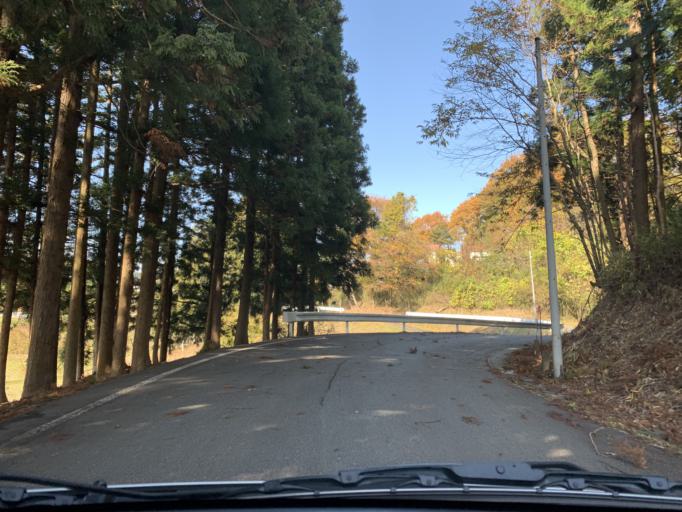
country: JP
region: Iwate
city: Ichinoseki
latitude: 39.0196
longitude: 141.1174
